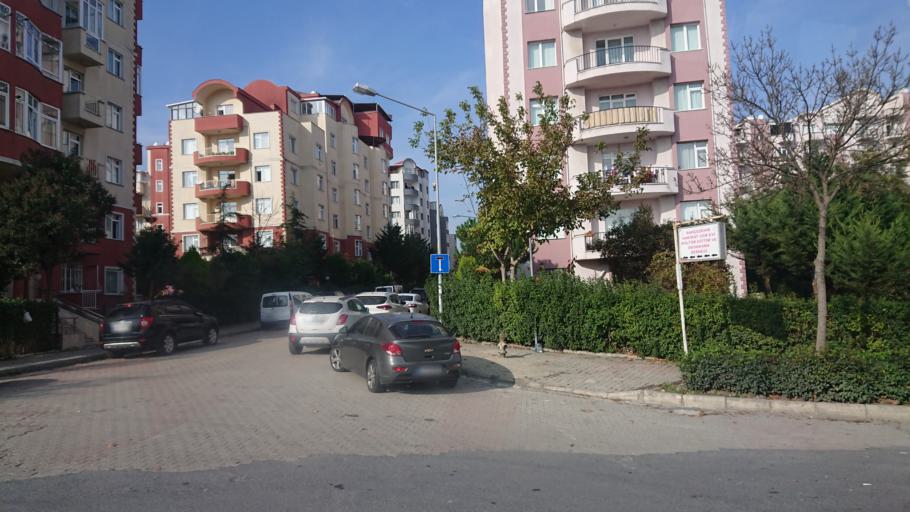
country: TR
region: Istanbul
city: Esenyurt
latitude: 41.0723
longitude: 28.6665
